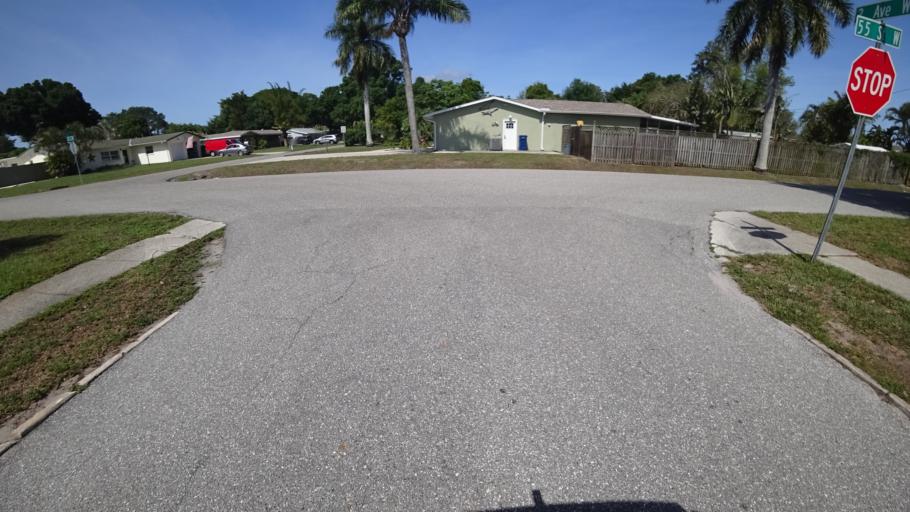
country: US
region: Florida
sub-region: Manatee County
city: West Bradenton
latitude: 27.4983
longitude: -82.6161
